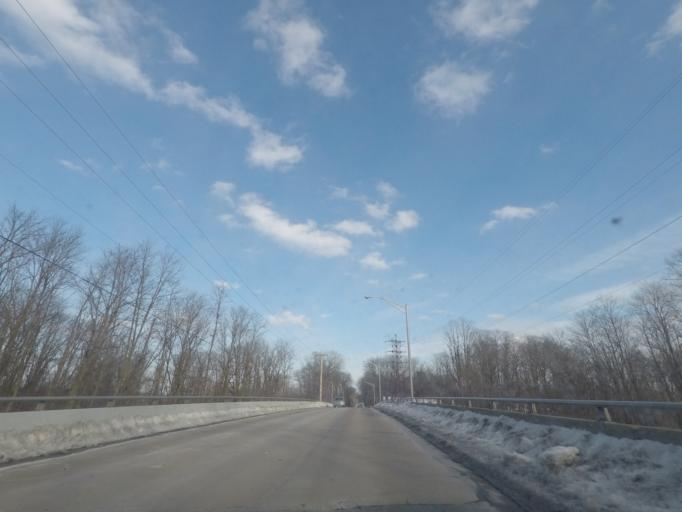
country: US
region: New York
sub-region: Schenectady County
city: Scotia
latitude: 42.8299
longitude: -73.9487
